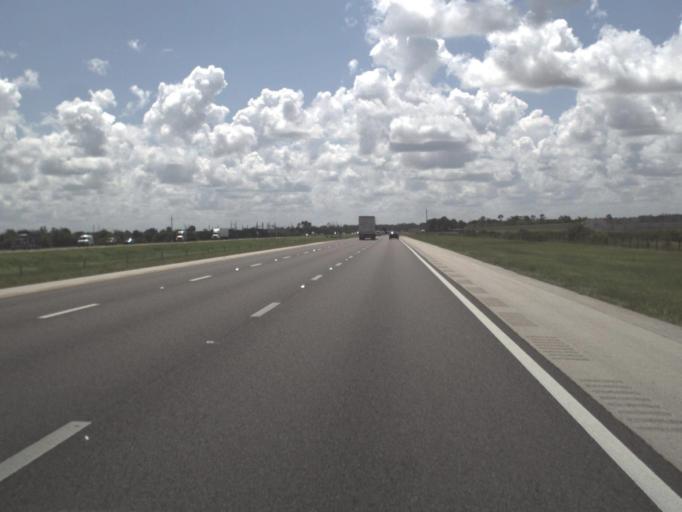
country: US
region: Florida
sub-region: Lee County
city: Bonita Springs
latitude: 26.3652
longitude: -81.7658
